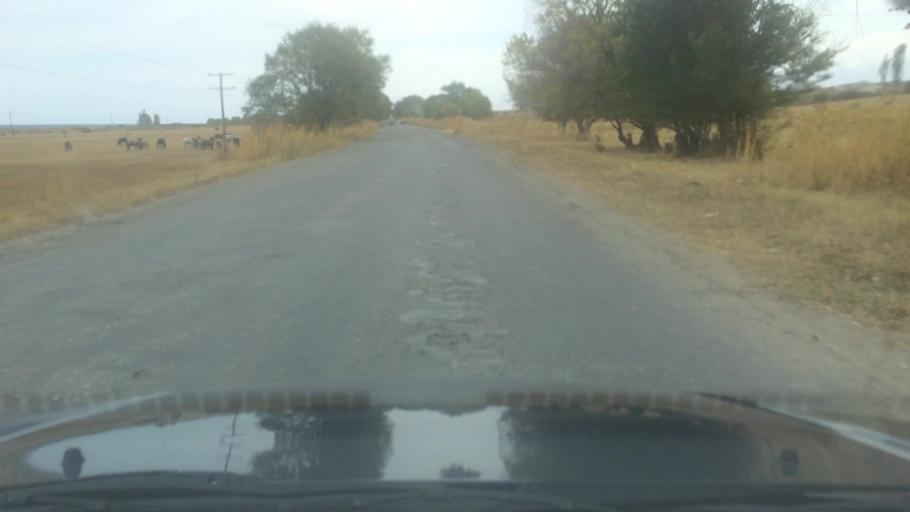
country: KG
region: Ysyk-Koel
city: Balykchy
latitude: 42.3074
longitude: 76.4666
